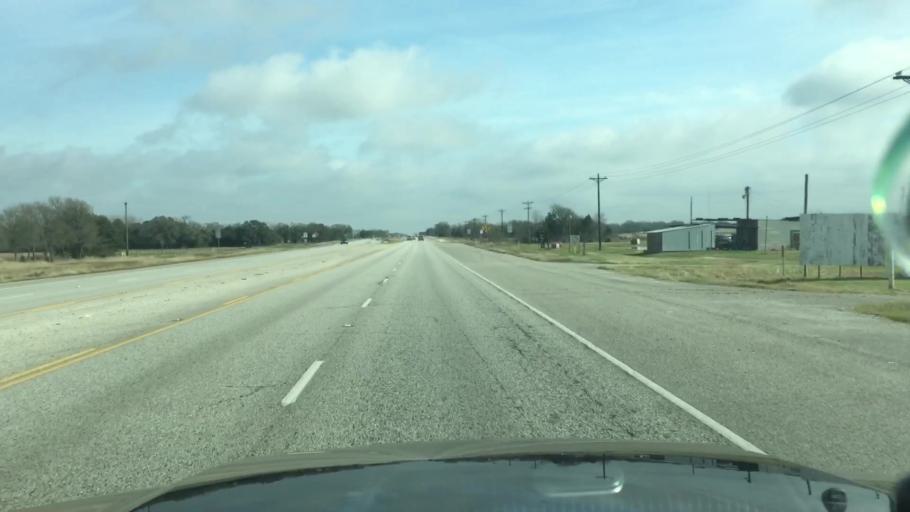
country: US
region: Texas
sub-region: Lee County
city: Giddings
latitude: 30.1752
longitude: -96.8910
